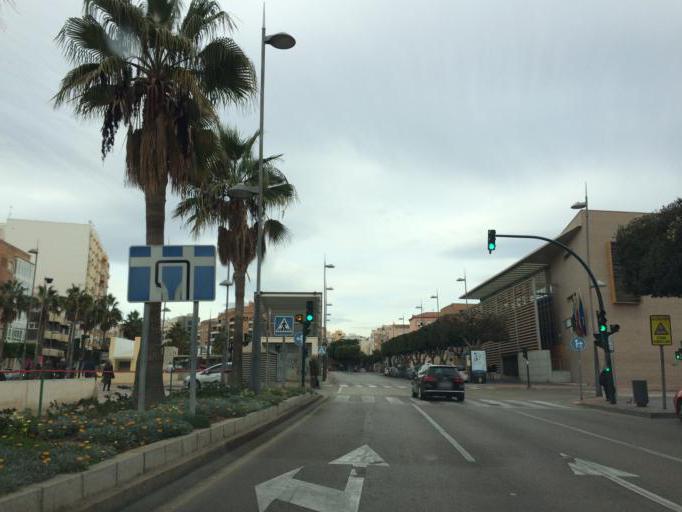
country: ES
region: Andalusia
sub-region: Provincia de Almeria
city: Almeria
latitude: 36.8421
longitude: -2.4577
